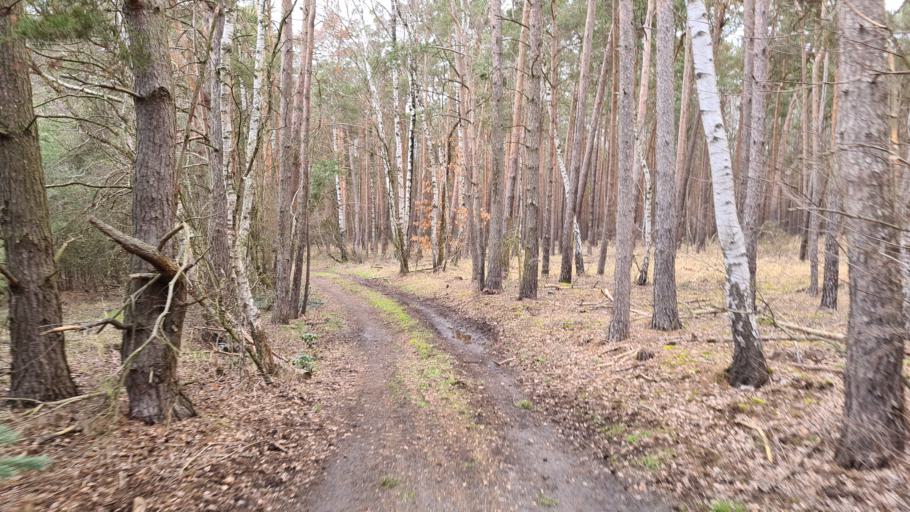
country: DE
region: Brandenburg
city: Schilda
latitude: 51.6098
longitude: 13.4035
